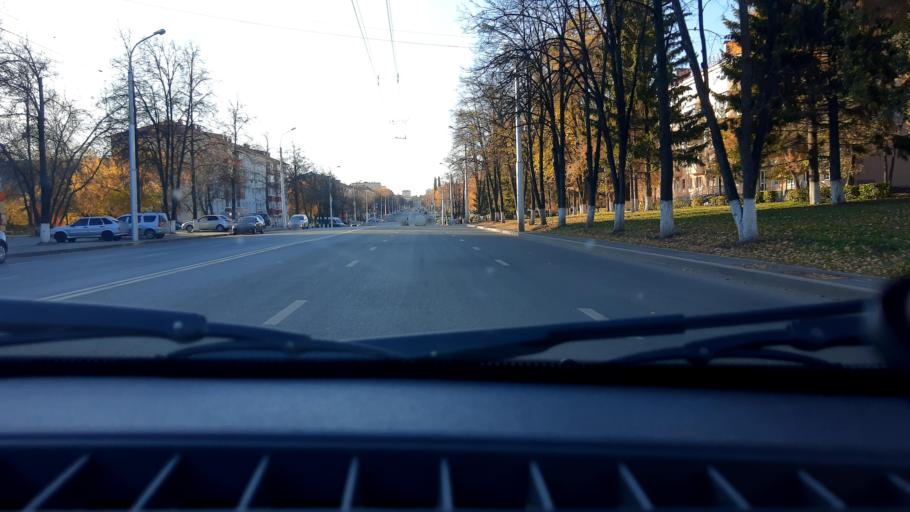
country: RU
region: Bashkortostan
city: Ufa
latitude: 54.8094
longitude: 56.1036
